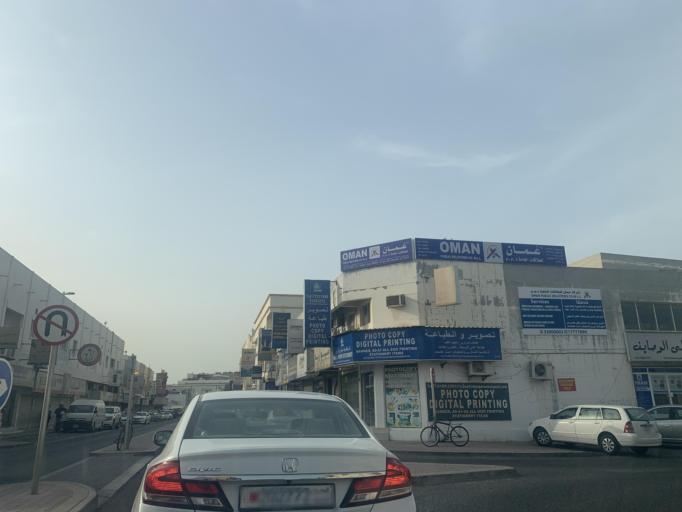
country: BH
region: Northern
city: Ar Rifa'
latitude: 26.1315
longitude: 50.5536
